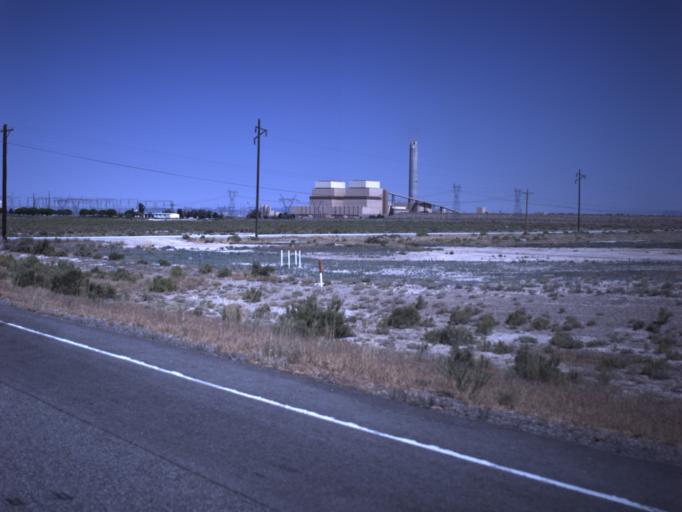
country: US
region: Utah
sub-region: Millard County
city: Delta
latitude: 39.4918
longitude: -112.5641
